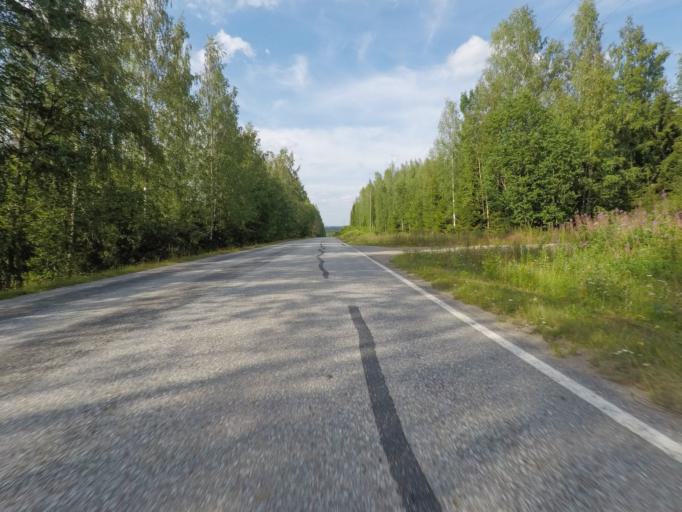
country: FI
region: Southern Savonia
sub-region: Savonlinna
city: Sulkava
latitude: 61.7106
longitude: 28.2104
